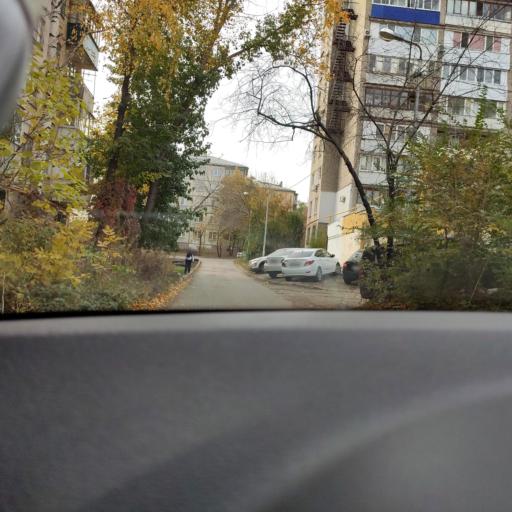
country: RU
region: Samara
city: Samara
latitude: 53.1912
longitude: 50.2017
